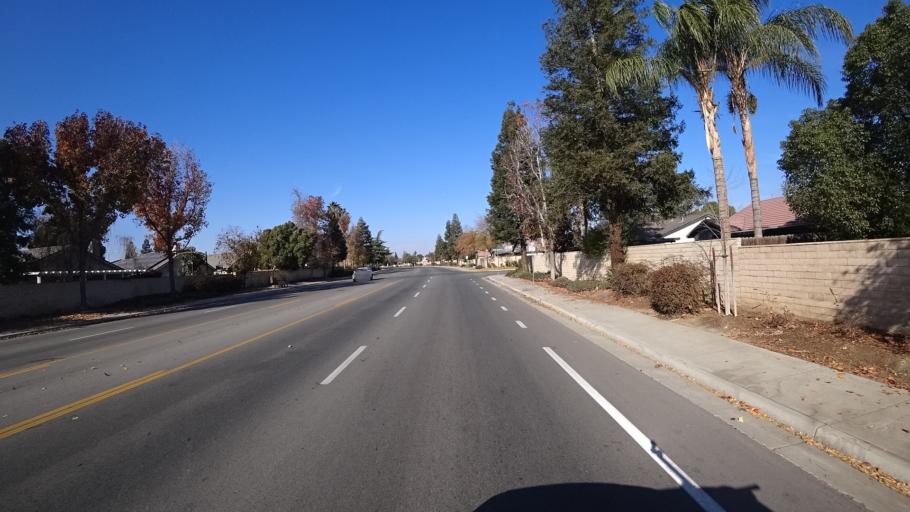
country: US
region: California
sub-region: Kern County
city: Greenacres
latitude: 35.3881
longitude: -119.1010
